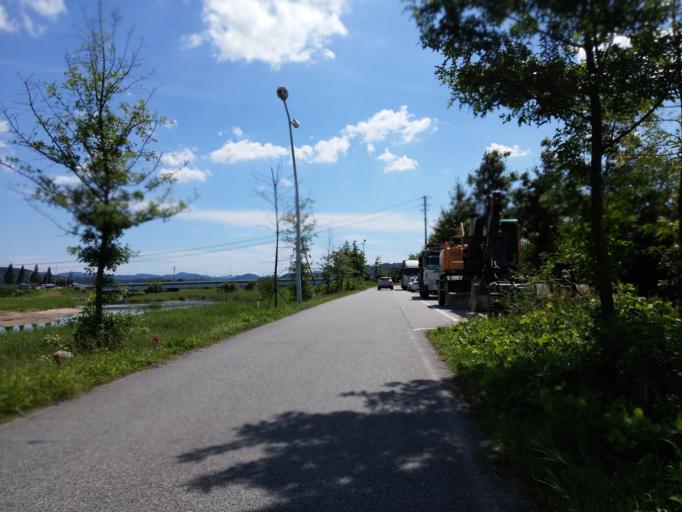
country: KR
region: Chungcheongbuk-do
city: Cheongju-si
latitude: 36.5999
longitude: 127.4972
